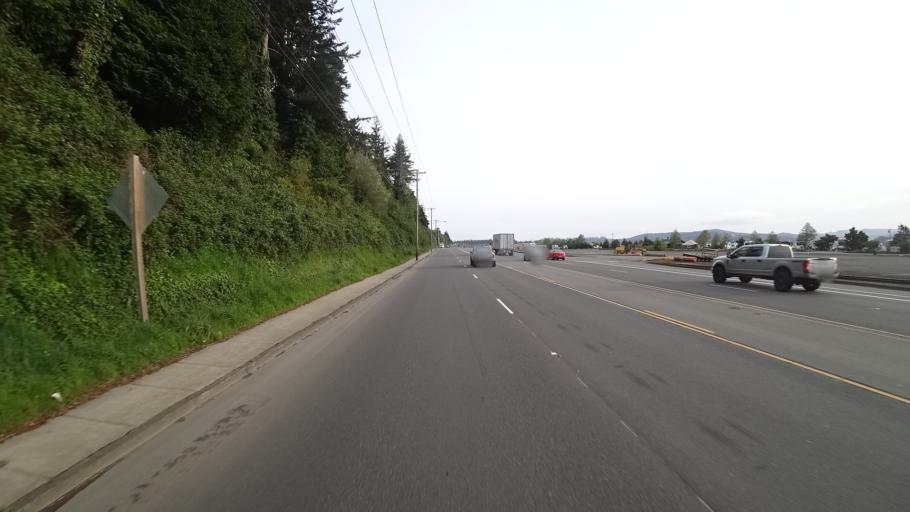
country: US
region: Oregon
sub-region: Coos County
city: North Bend
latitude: 43.3964
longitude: -124.2203
